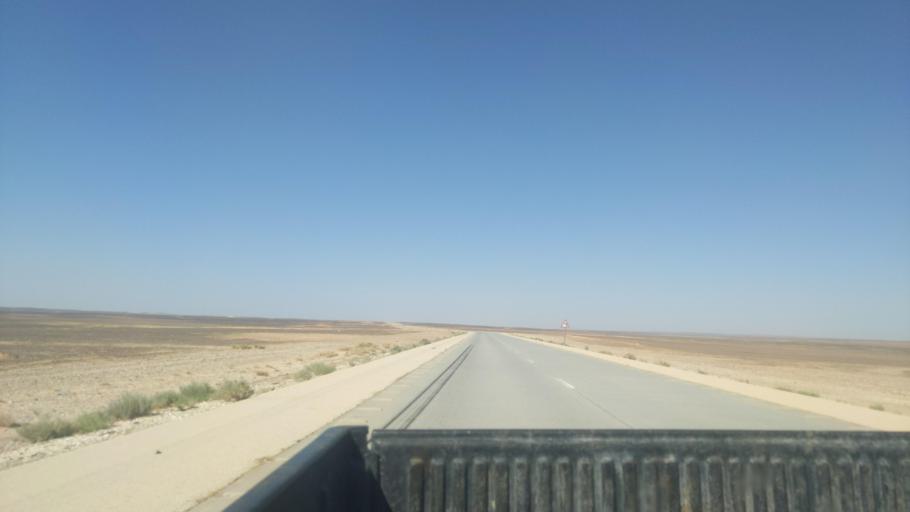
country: JO
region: Amman
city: Al Azraq ash Shamali
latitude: 31.4498
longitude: 36.7698
